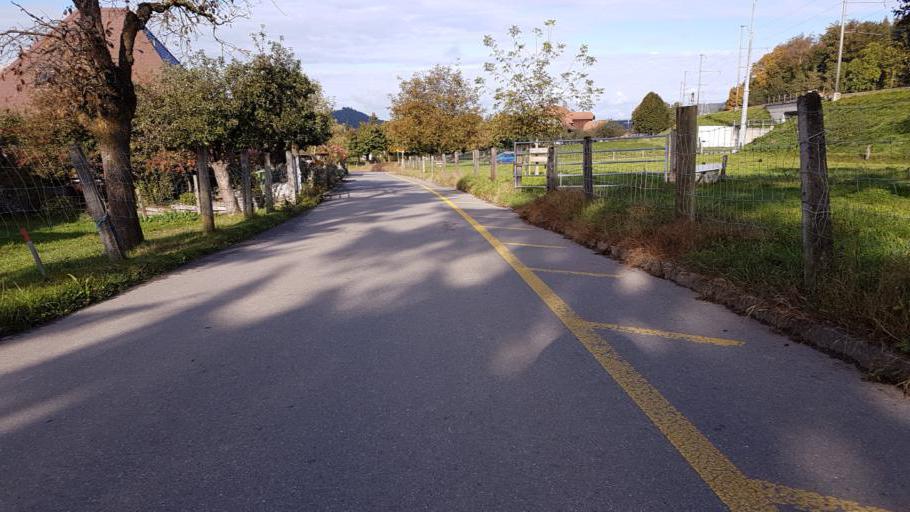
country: CH
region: Bern
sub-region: Bern-Mittelland District
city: Worb
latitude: 46.9153
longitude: 7.5530
